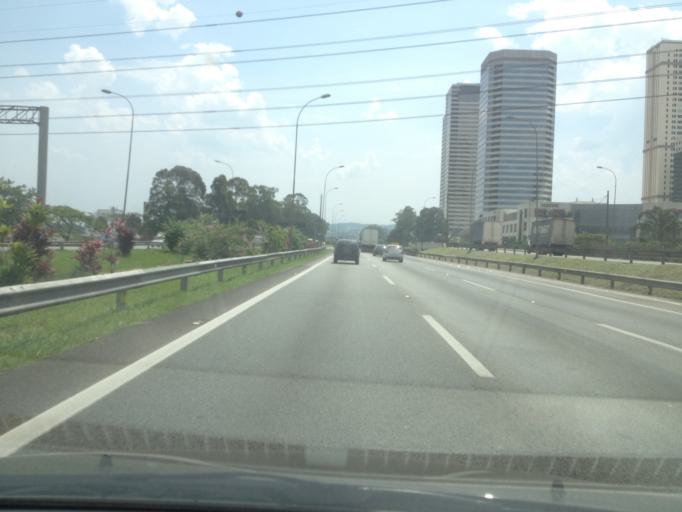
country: BR
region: Sao Paulo
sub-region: Carapicuiba
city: Carapicuiba
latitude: -23.5061
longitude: -46.8450
